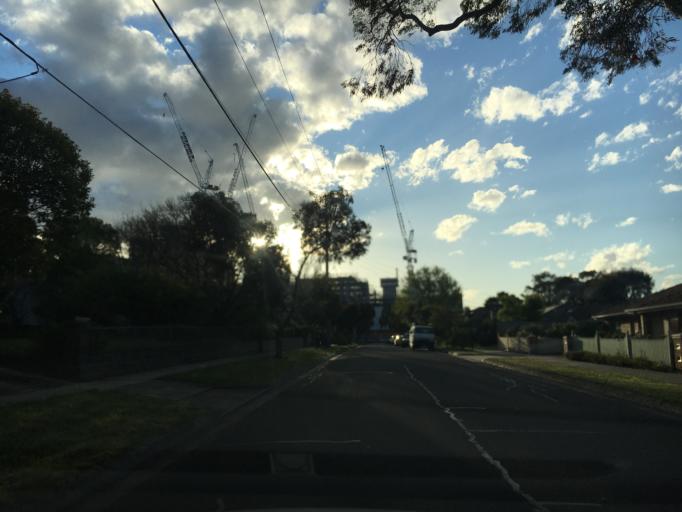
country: AU
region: Victoria
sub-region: Whitehorse
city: Vermont South
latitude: -37.8779
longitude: 145.1685
